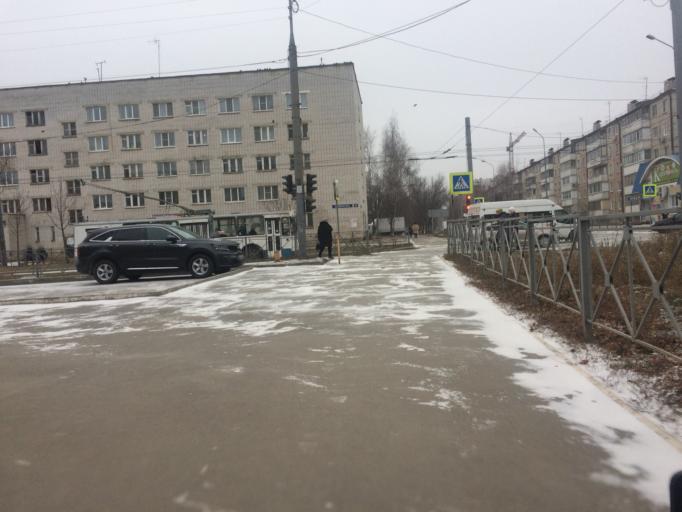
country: RU
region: Mariy-El
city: Yoshkar-Ola
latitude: 56.6502
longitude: 47.8641
